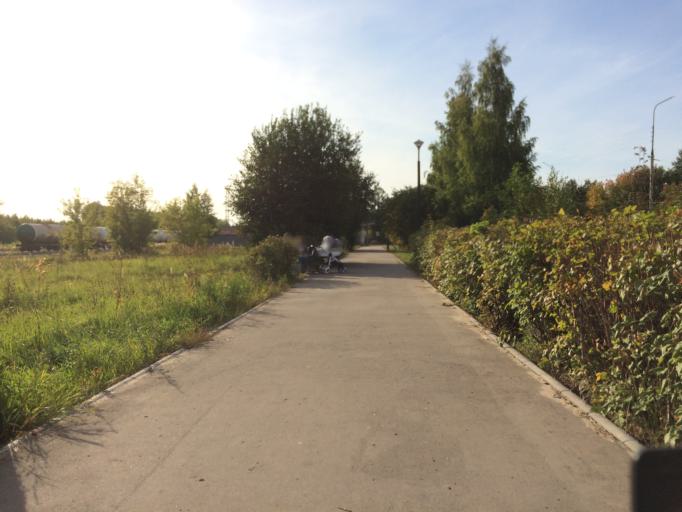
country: RU
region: Mariy-El
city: Medvedevo
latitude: 56.6281
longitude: 47.8105
